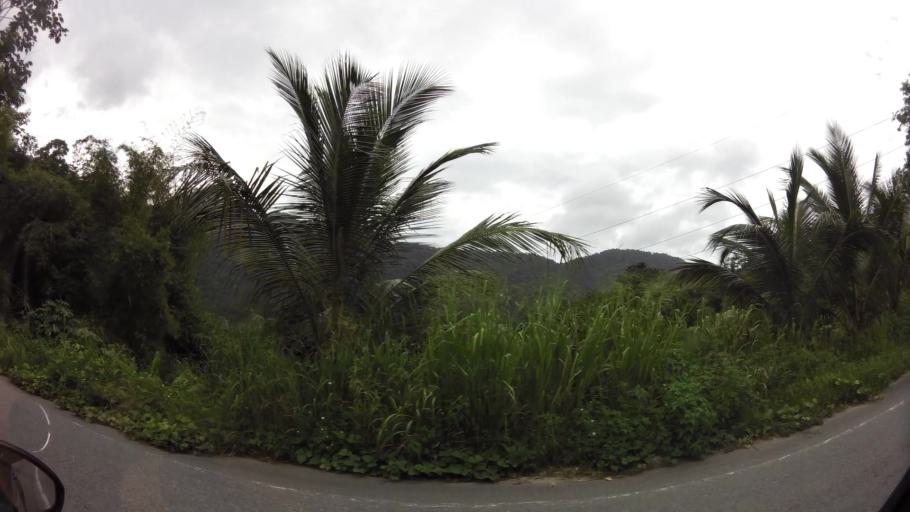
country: TT
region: Diego Martin
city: Petit Valley
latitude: 10.7605
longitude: -61.4448
